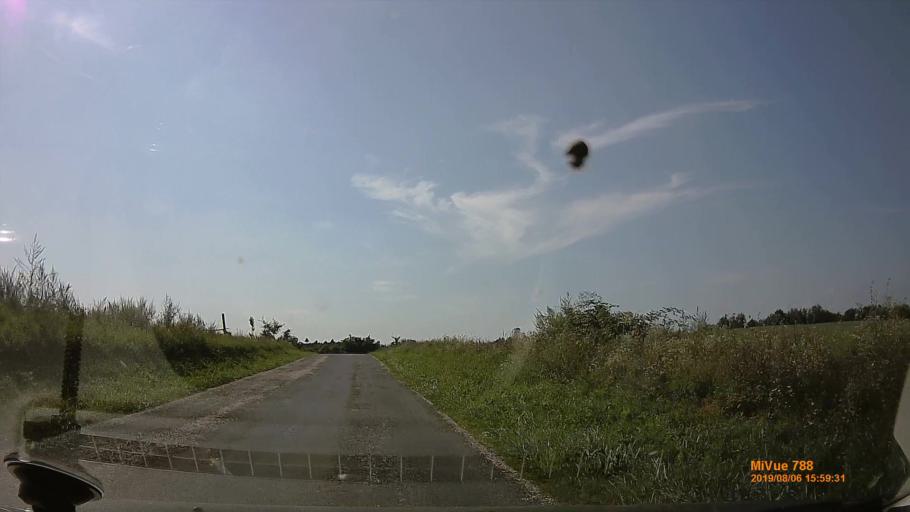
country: HR
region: Koprivnicko-Krizevacka
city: Drnje
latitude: 46.2943
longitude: 16.9915
